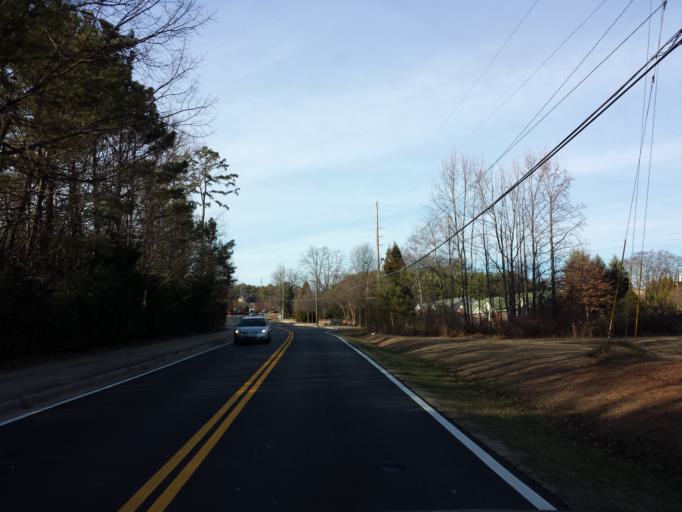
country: US
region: Georgia
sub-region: Cobb County
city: Marietta
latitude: 33.9750
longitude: -84.5663
